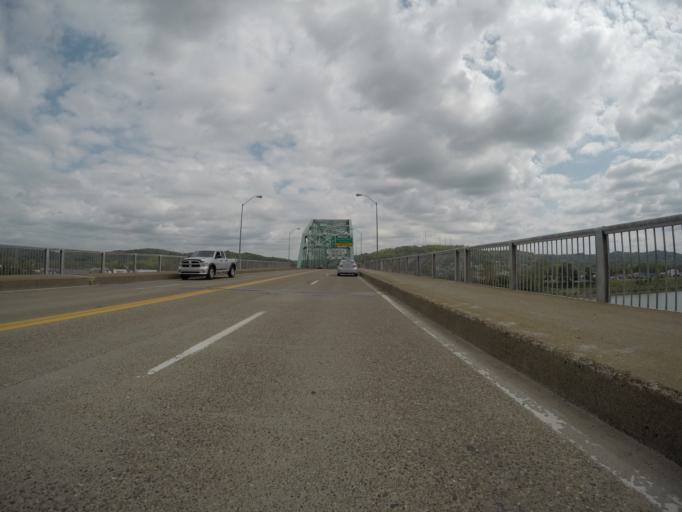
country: US
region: West Virginia
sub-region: Kanawha County
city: South Charleston
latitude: 38.3650
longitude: -81.6693
